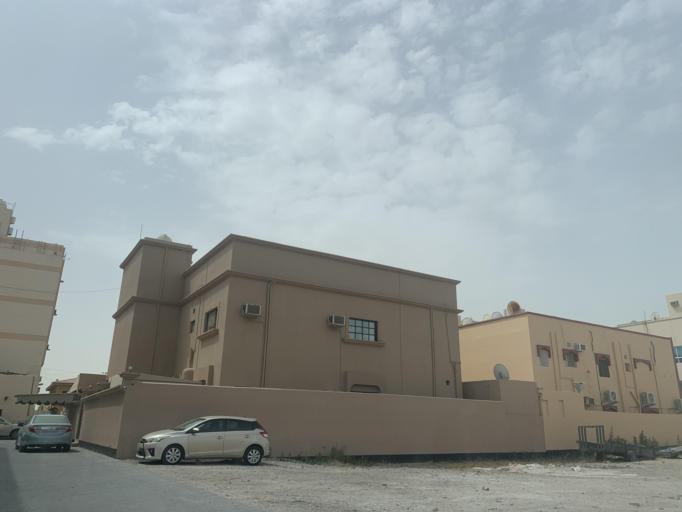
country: BH
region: Northern
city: Ar Rifa'
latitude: 26.1273
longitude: 50.5626
